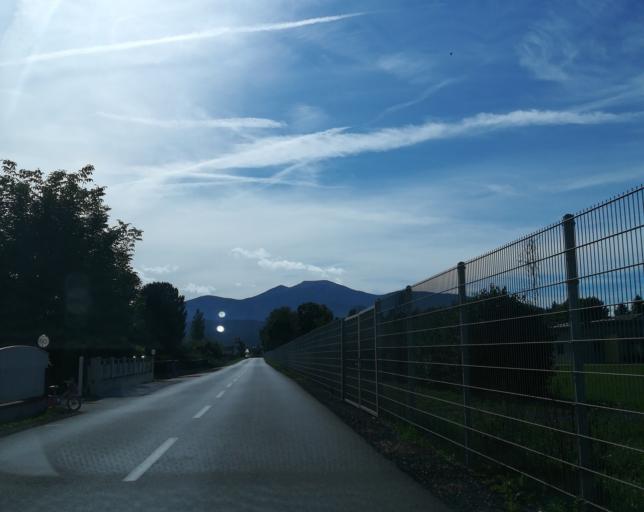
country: AT
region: Styria
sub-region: Politischer Bezirk Murtal
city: Flatschach
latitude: 47.2009
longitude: 14.7630
